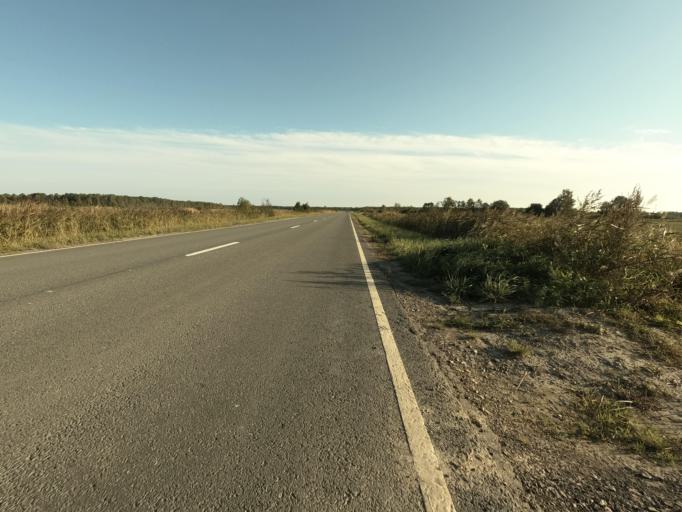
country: RU
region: St.-Petersburg
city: Sapernyy
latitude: 59.7394
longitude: 30.6520
